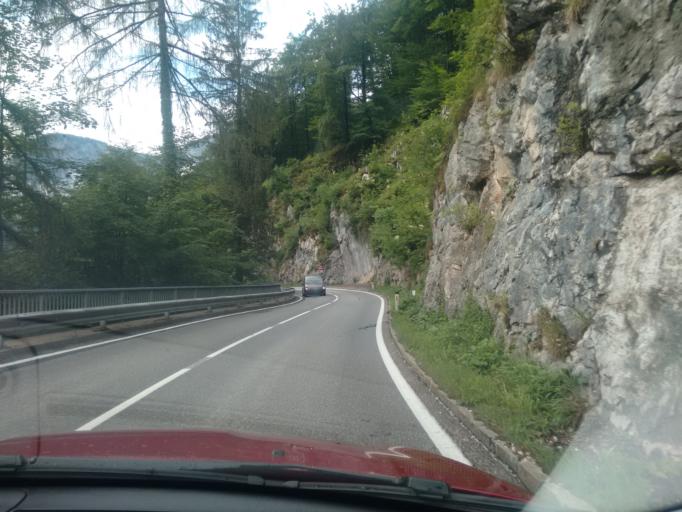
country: AT
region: Upper Austria
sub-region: Politischer Bezirk Gmunden
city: Bad Goisern
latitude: 47.5815
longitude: 13.6563
